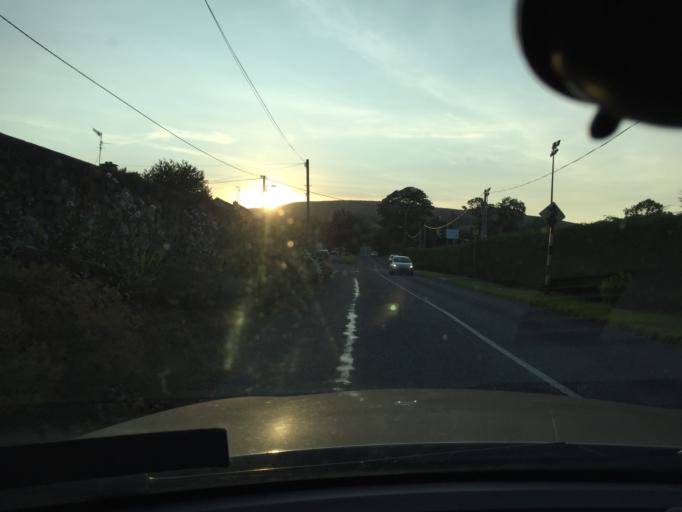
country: IE
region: Leinster
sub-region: Wicklow
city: Enniskerry
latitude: 53.1927
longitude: -6.1813
